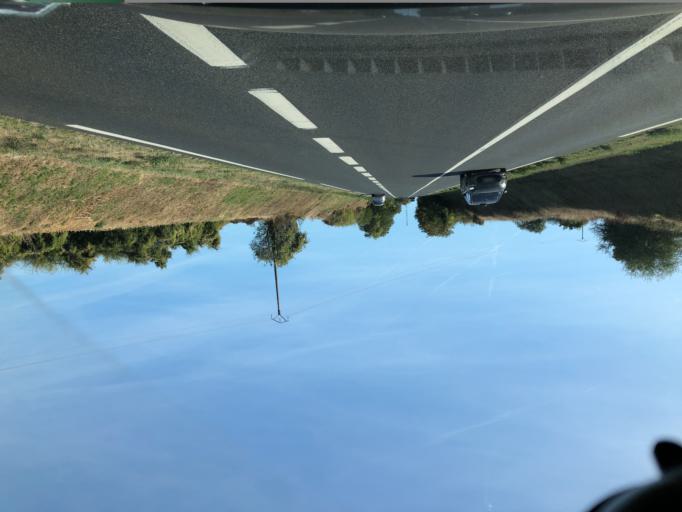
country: FR
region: Ile-de-France
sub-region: Departement de l'Essonne
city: Morigny-Champigny
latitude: 48.4303
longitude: 2.1844
